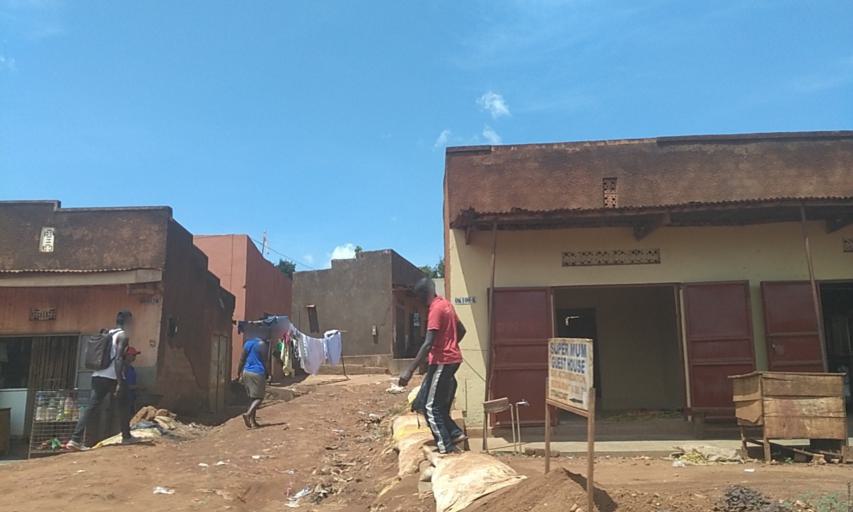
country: UG
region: Central Region
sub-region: Wakiso District
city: Wakiso
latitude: 0.3984
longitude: 32.4821
